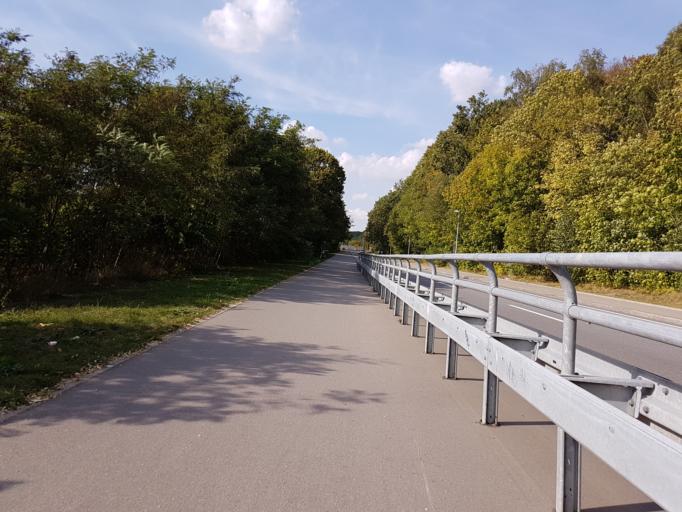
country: DE
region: Saxony
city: Taura
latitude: 50.9221
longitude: 12.8576
